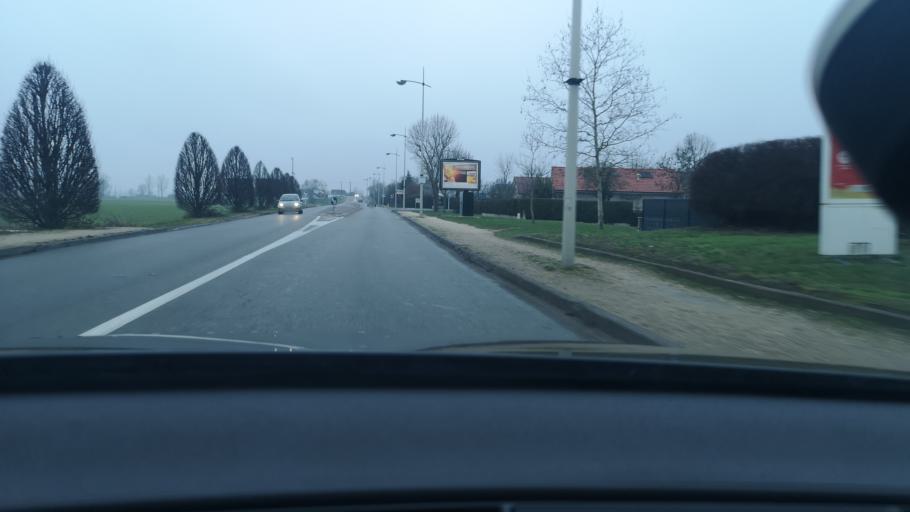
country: FR
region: Bourgogne
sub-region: Departement de la Cote-d'Or
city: Longvic
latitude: 47.2804
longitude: 5.0627
